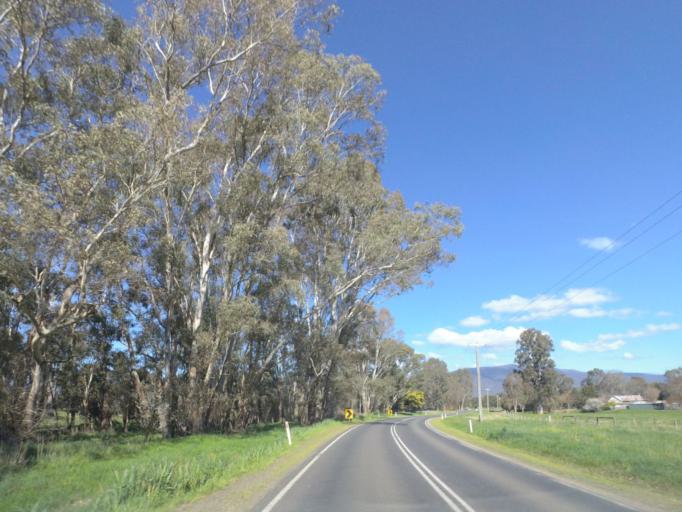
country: AU
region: Victoria
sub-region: Murrindindi
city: Alexandra
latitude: -37.2476
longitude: 145.7830
